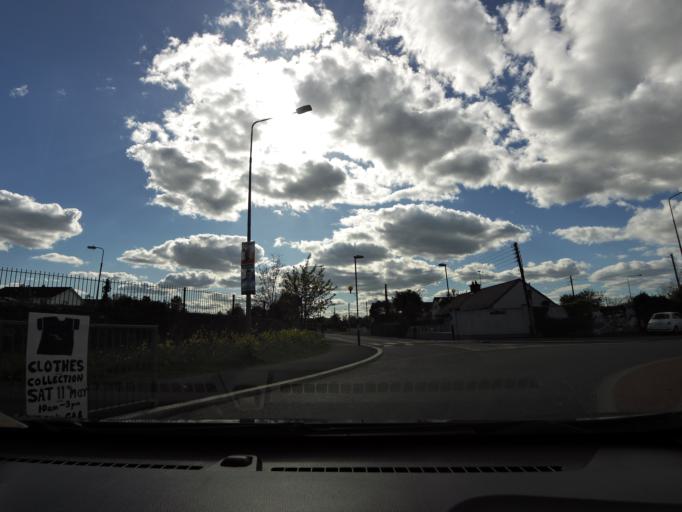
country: IE
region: Leinster
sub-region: Kildare
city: Kilcock
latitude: 53.3968
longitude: -6.6750
